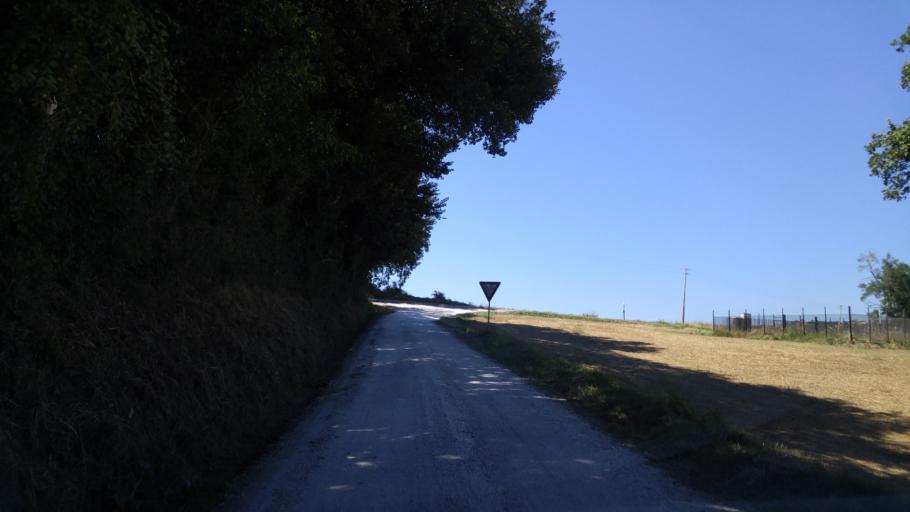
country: IT
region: The Marches
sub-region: Provincia di Pesaro e Urbino
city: Mombaroccio
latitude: 43.8313
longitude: 12.8873
